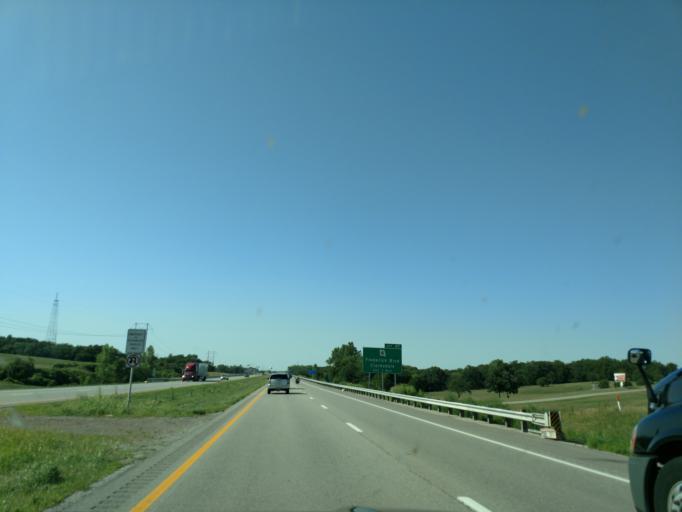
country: US
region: Missouri
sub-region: Buchanan County
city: Saint Joseph
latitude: 39.7590
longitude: -94.7909
